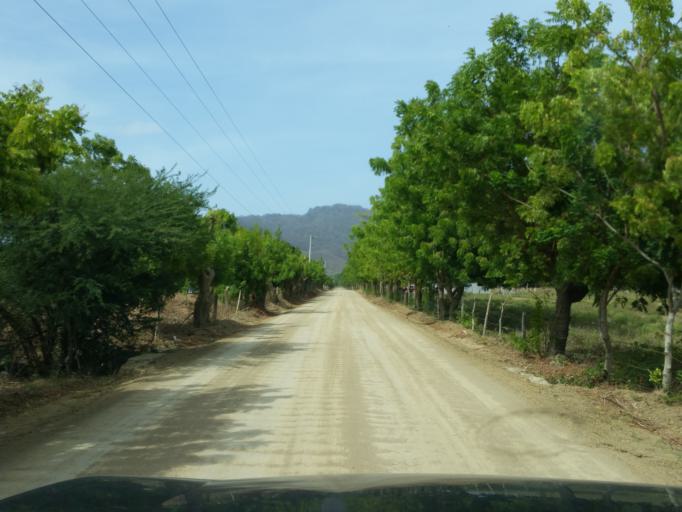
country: NI
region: Rivas
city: Tola
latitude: 11.4238
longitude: -86.0304
